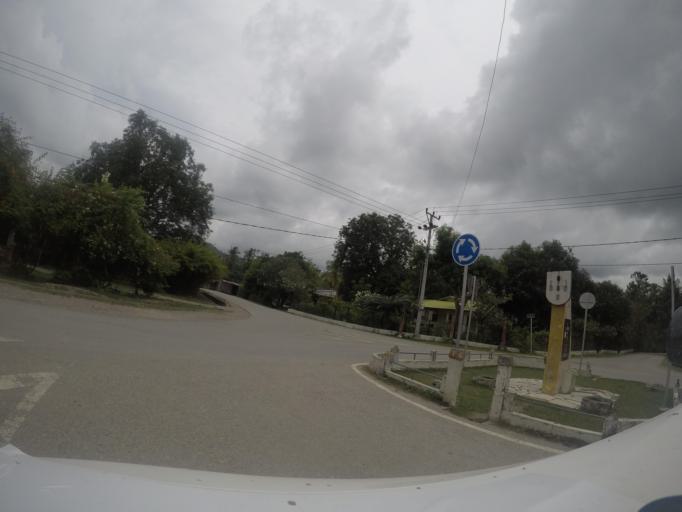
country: TL
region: Viqueque
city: Viqueque
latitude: -8.8695
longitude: 126.3667
